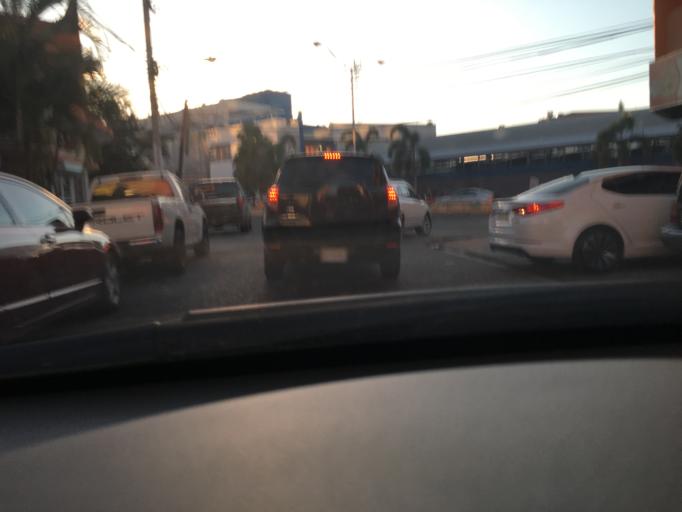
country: DO
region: Nacional
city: San Carlos
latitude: 18.4764
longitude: -69.9065
